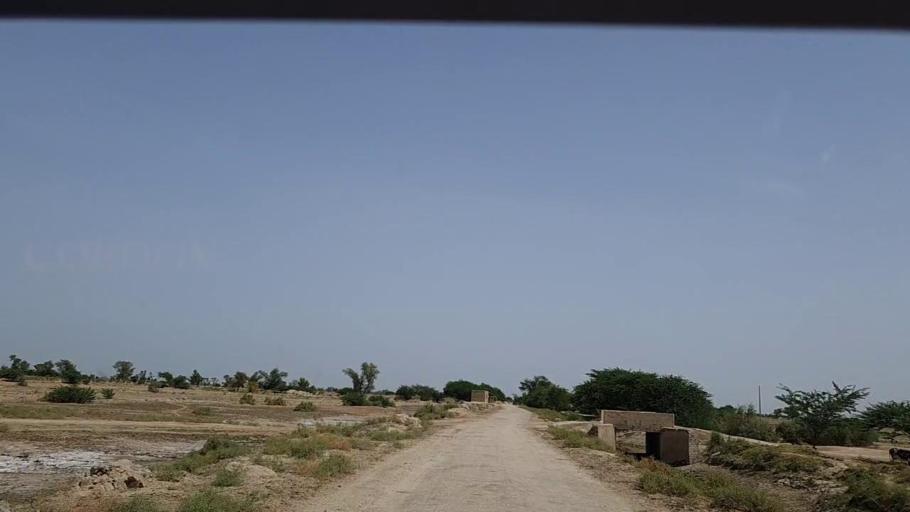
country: PK
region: Sindh
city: Johi
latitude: 26.7748
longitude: 67.6249
